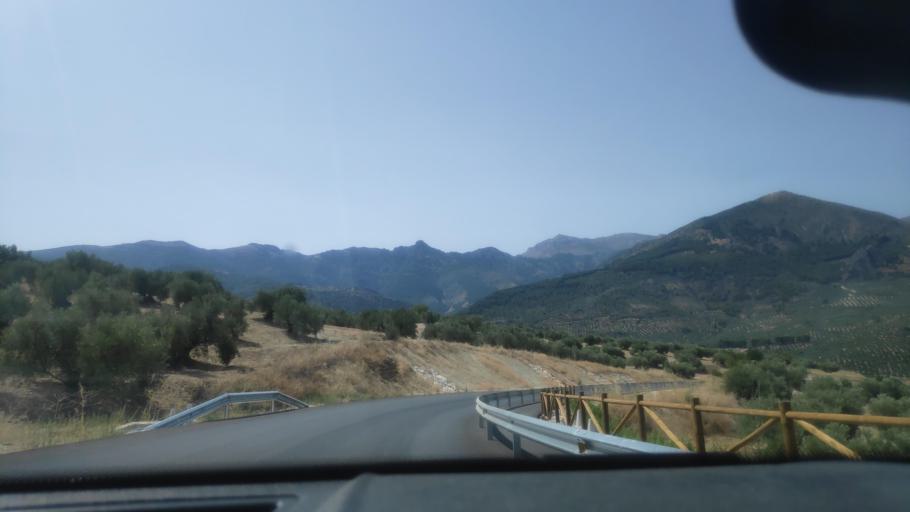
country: ES
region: Andalusia
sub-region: Provincia de Jaen
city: Jodar
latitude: 37.8121
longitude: -3.4125
